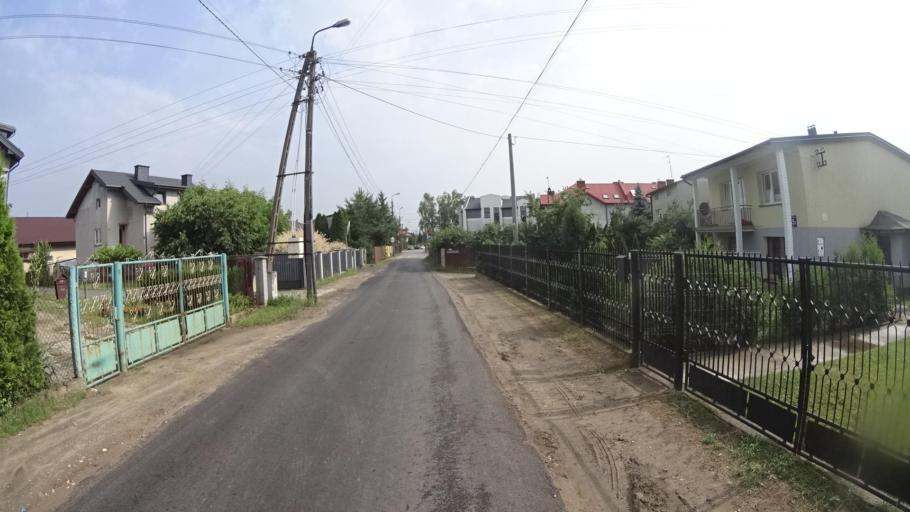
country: PL
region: Masovian Voivodeship
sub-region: Powiat pruszkowski
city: Raszyn
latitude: 52.1646
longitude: 20.9201
